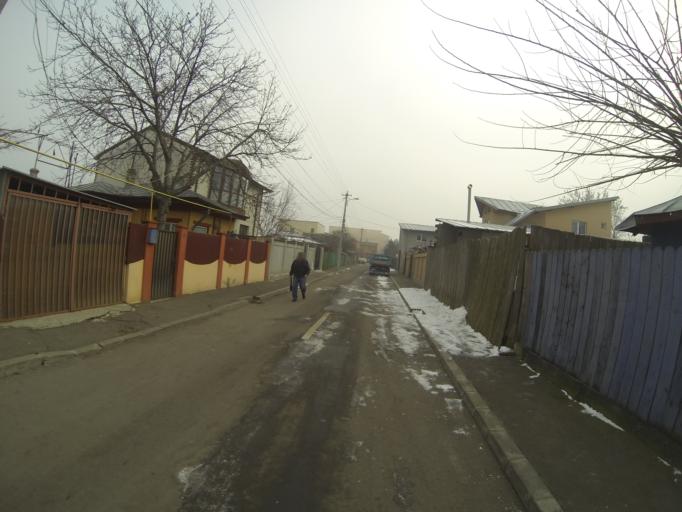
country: RO
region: Bucuresti
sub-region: Municipiul Bucuresti
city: Bucuresti
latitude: 44.3957
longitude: 26.0710
